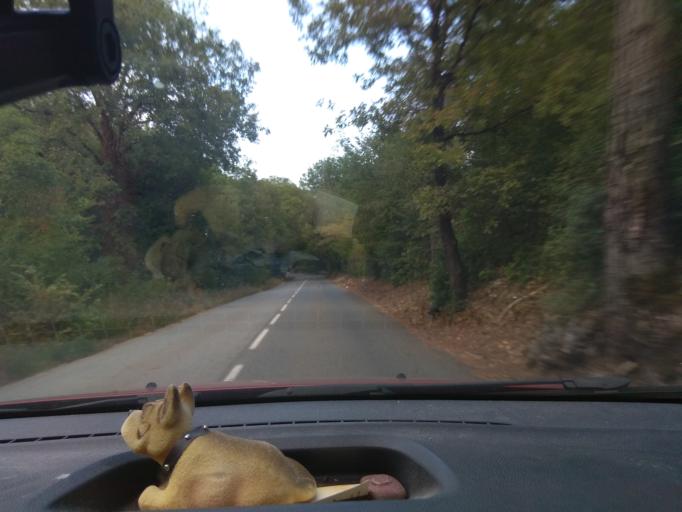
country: FR
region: Provence-Alpes-Cote d'Azur
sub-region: Departement des Alpes-Maritimes
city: Le Rouret
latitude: 43.6797
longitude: 7.0492
